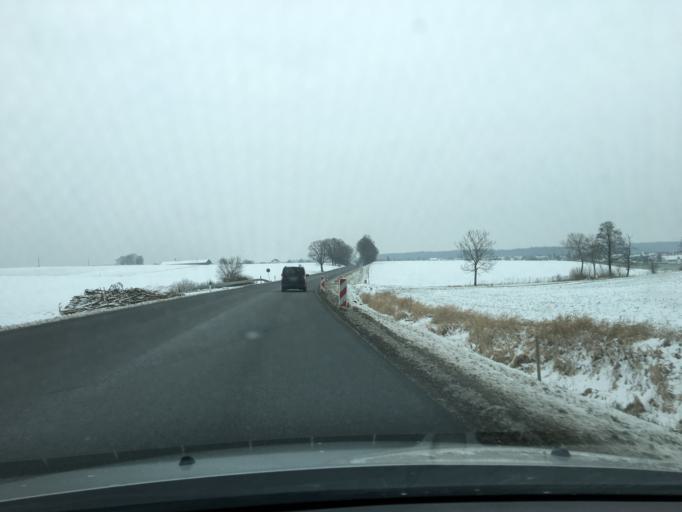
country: DE
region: Bavaria
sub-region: Lower Bavaria
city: Furth
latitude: 48.4183
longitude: 12.4153
